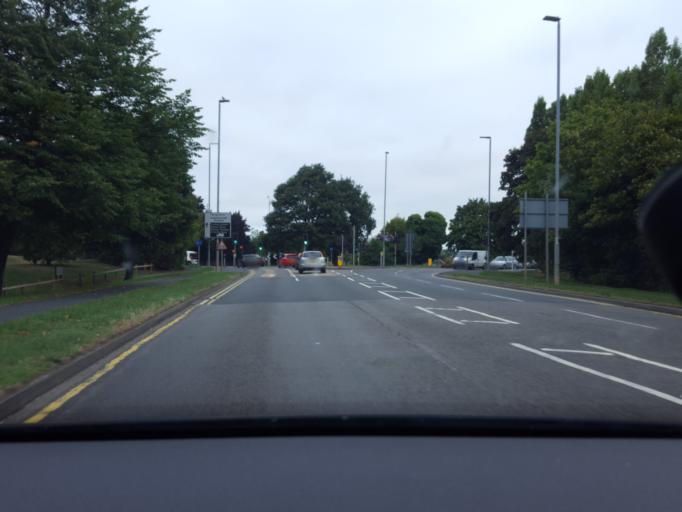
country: GB
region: England
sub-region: Leicestershire
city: Loughborough
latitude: 52.7698
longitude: -1.2252
